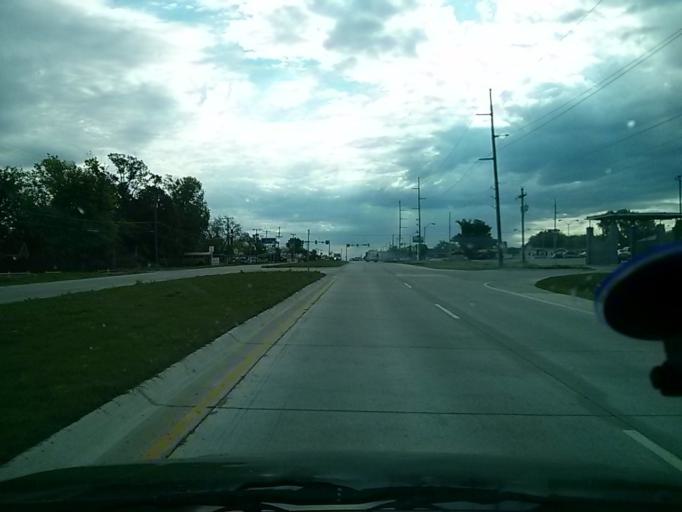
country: US
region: Oklahoma
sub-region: Tulsa County
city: Owasso
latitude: 36.1606
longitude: -95.8538
